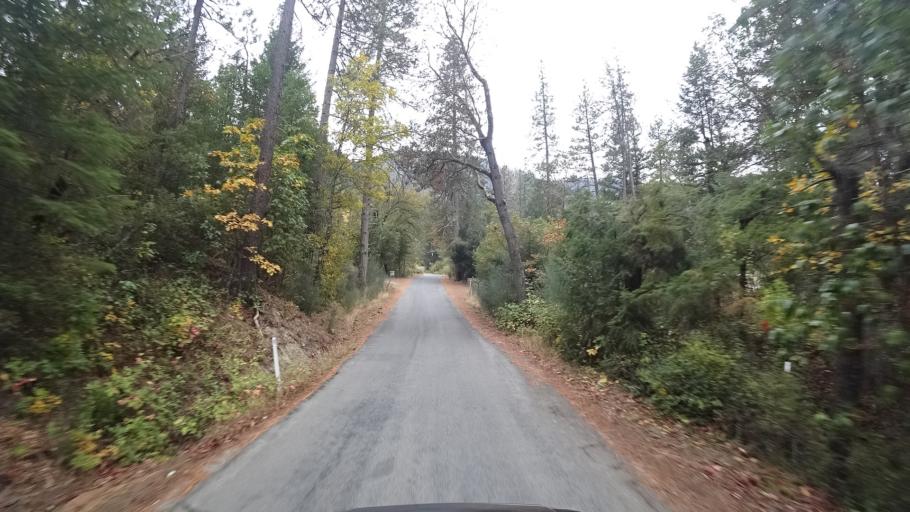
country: US
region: California
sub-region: Siskiyou County
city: Happy Camp
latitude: 41.8323
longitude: -123.1795
